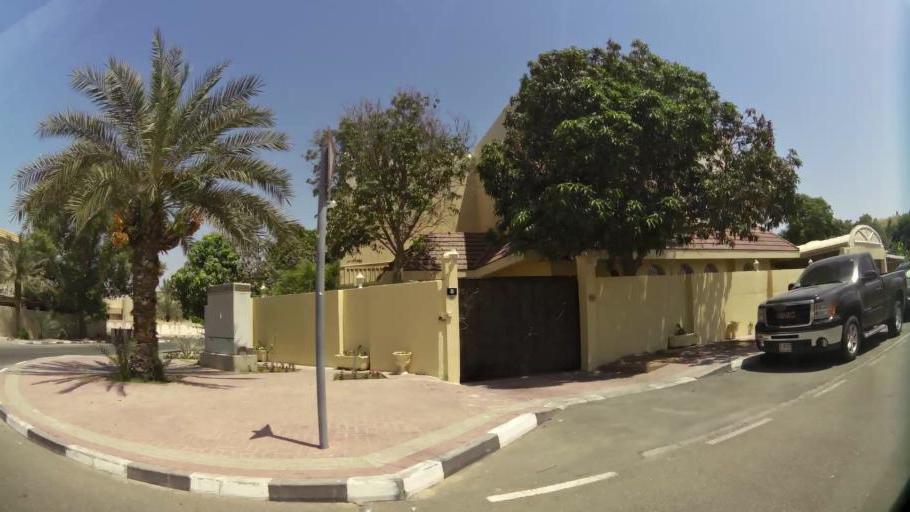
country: AE
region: Ash Shariqah
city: Sharjah
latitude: 25.2980
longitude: 55.3415
